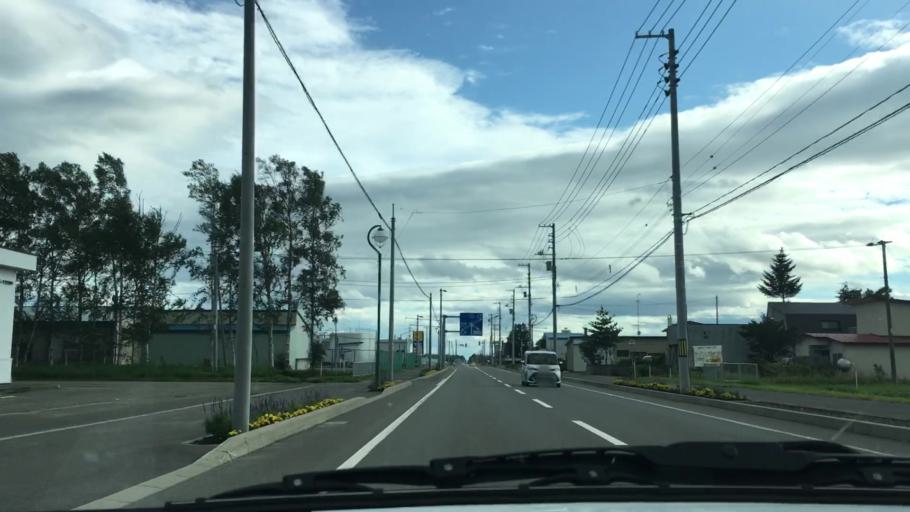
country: JP
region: Hokkaido
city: Otofuke
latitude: 43.2271
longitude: 143.2938
